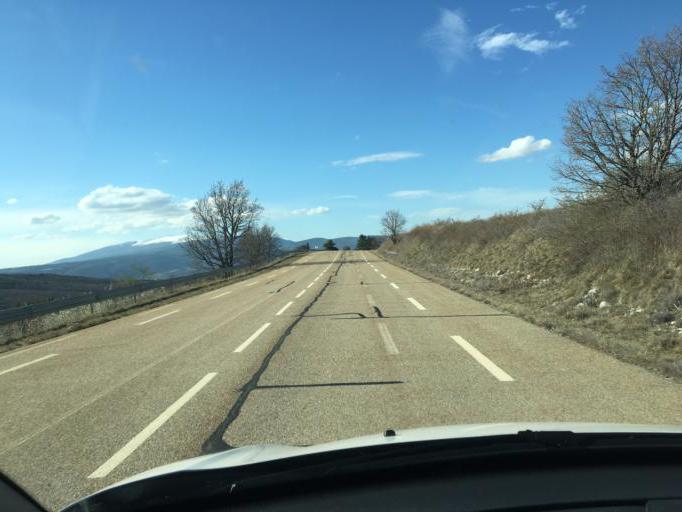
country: FR
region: Provence-Alpes-Cote d'Azur
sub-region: Departement du Vaucluse
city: Sault
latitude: 44.0480
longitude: 5.4427
